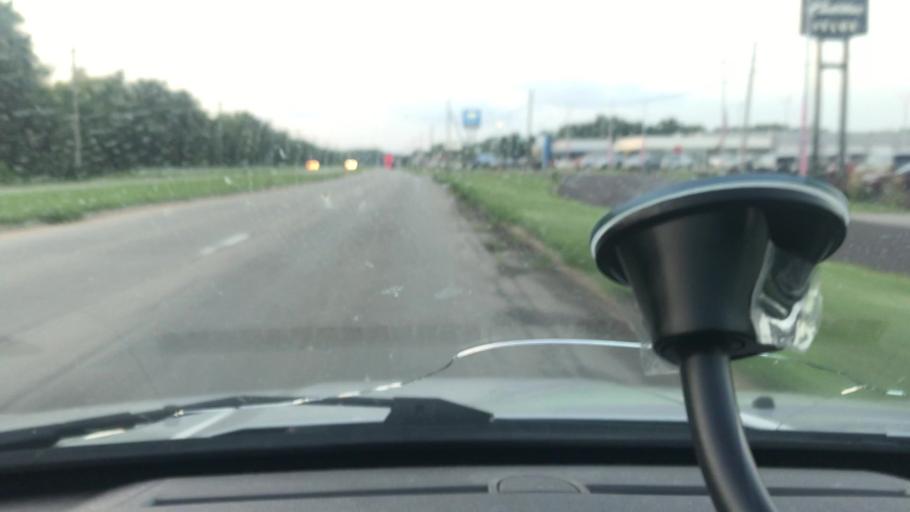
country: US
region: Illinois
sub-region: Tazewell County
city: North Pekin
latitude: 40.5985
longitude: -89.6390
